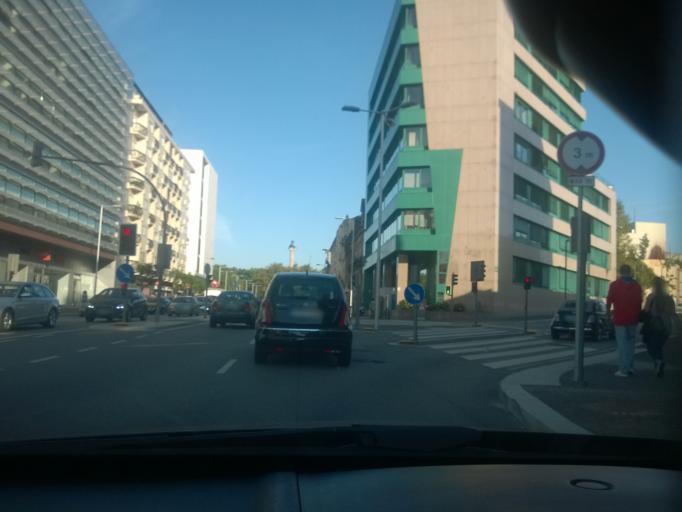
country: PT
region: Porto
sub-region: Porto
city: Porto
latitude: 41.1585
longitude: -8.6332
